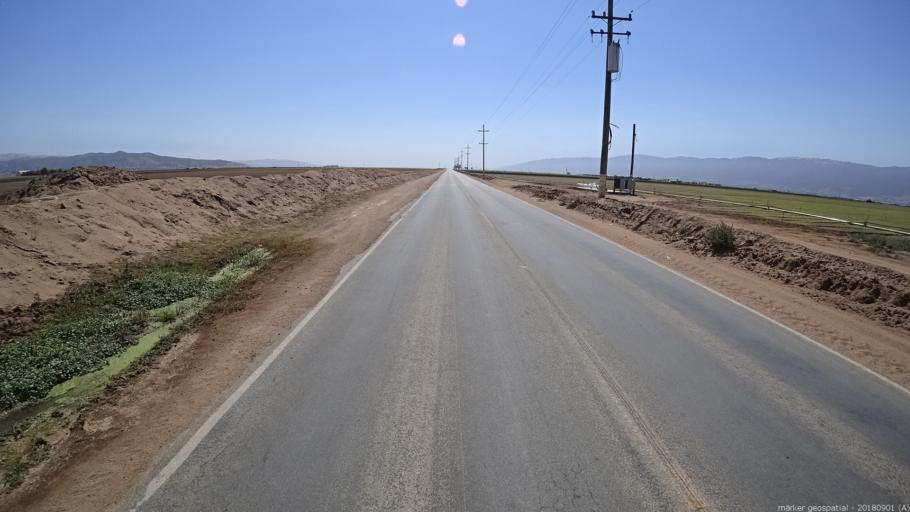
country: US
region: California
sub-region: Monterey County
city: Chualar
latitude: 36.5955
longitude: -121.5064
